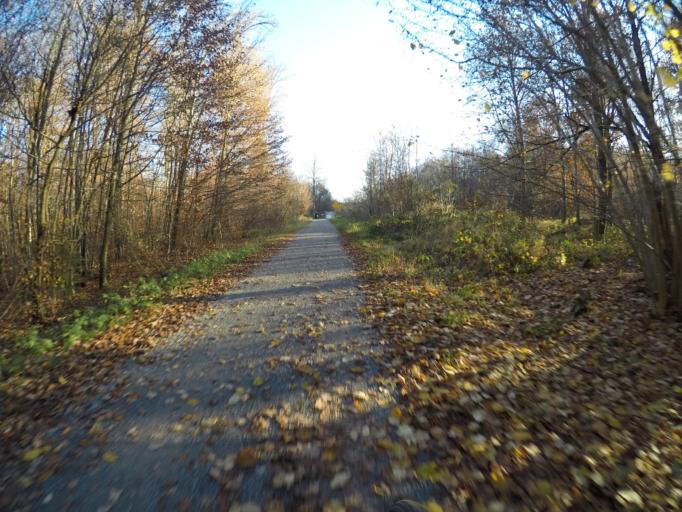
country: DE
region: Baden-Wuerttemberg
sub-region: Regierungsbezirk Stuttgart
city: Schonaich
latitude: 48.6933
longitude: 9.0523
